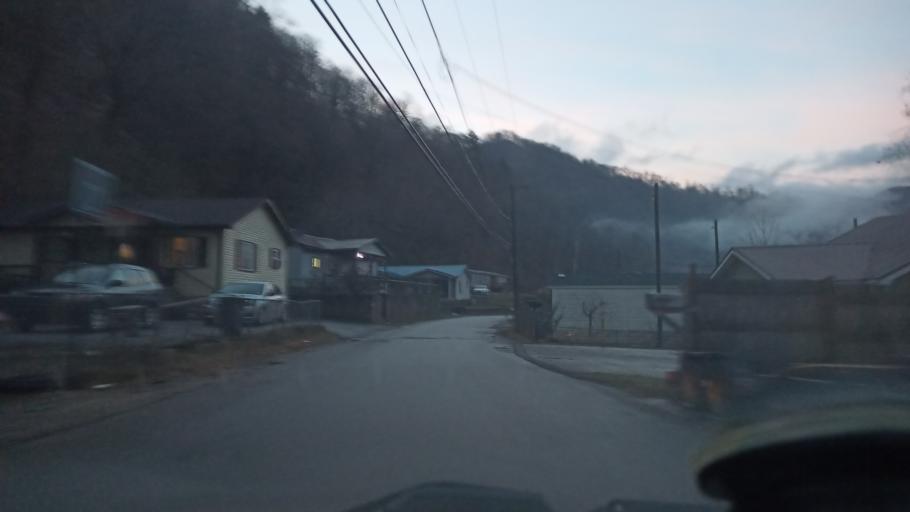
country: US
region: West Virginia
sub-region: Logan County
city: Mallory
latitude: 37.7247
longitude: -81.8760
